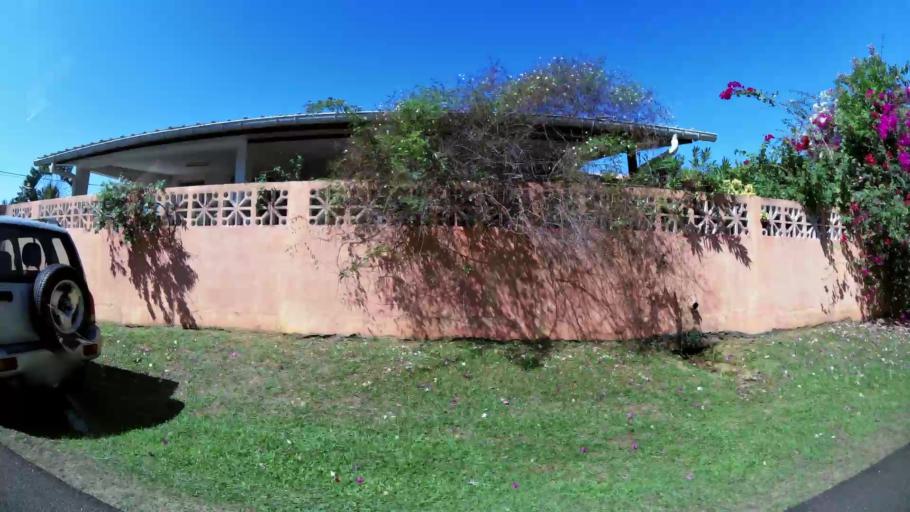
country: GF
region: Guyane
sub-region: Guyane
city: Remire-Montjoly
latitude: 4.9245
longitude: -52.2800
